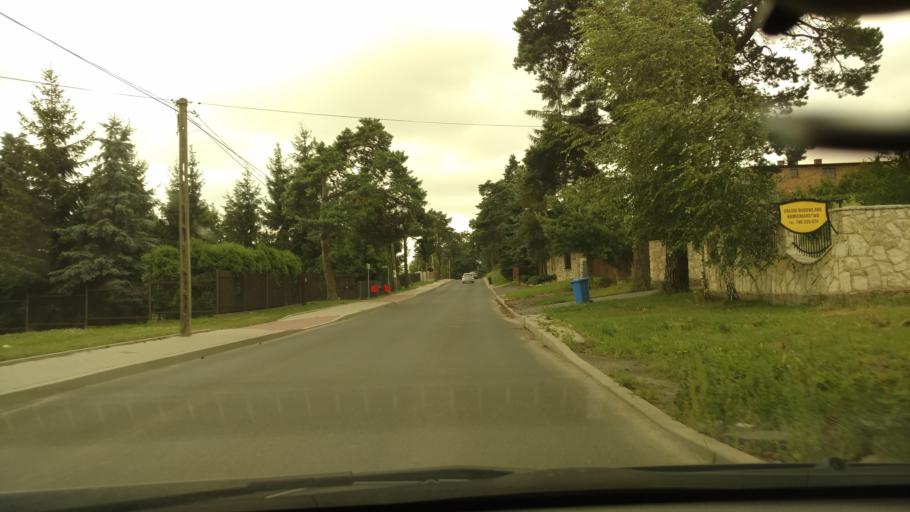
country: PL
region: Lesser Poland Voivodeship
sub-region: Powiat krakowski
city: Zielonki
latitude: 50.1229
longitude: 19.9398
